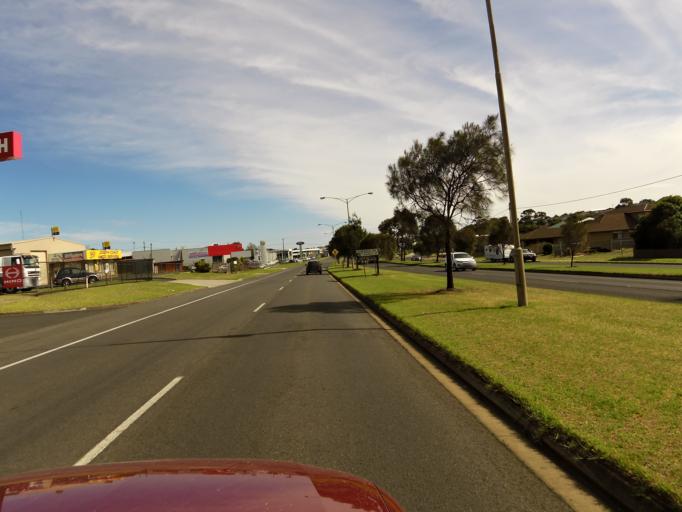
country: AU
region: Victoria
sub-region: Warrnambool
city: Warrnambool
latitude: -38.3707
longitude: 142.4709
